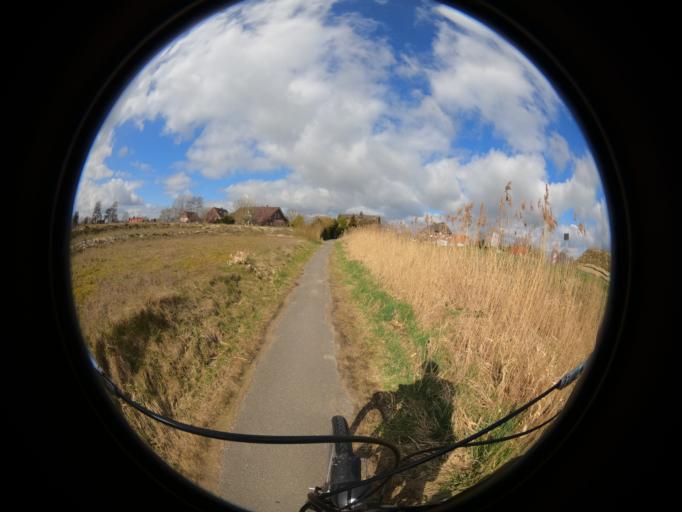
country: DE
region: Lower Saxony
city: Neu Wulmstorf
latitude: 53.4913
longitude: 9.7792
